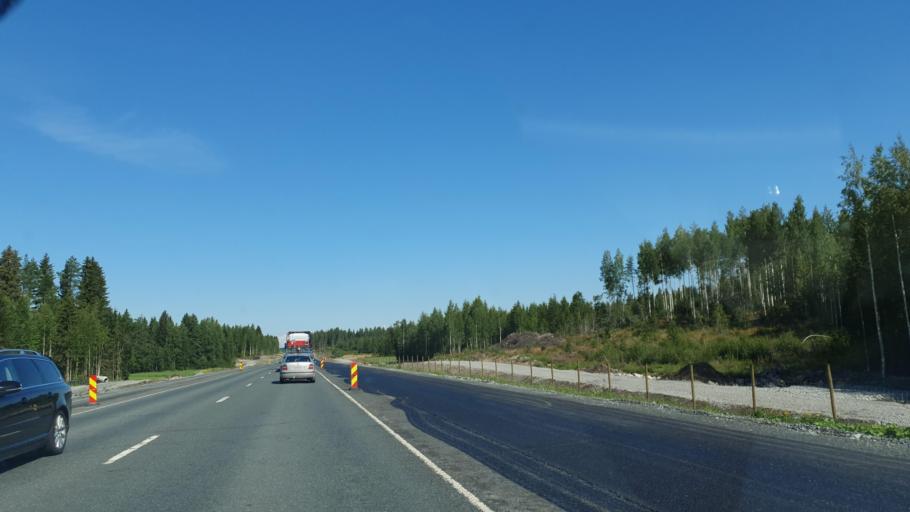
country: FI
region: Northern Savo
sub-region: Ylae-Savo
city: Lapinlahti
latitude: 63.2957
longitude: 27.4530
